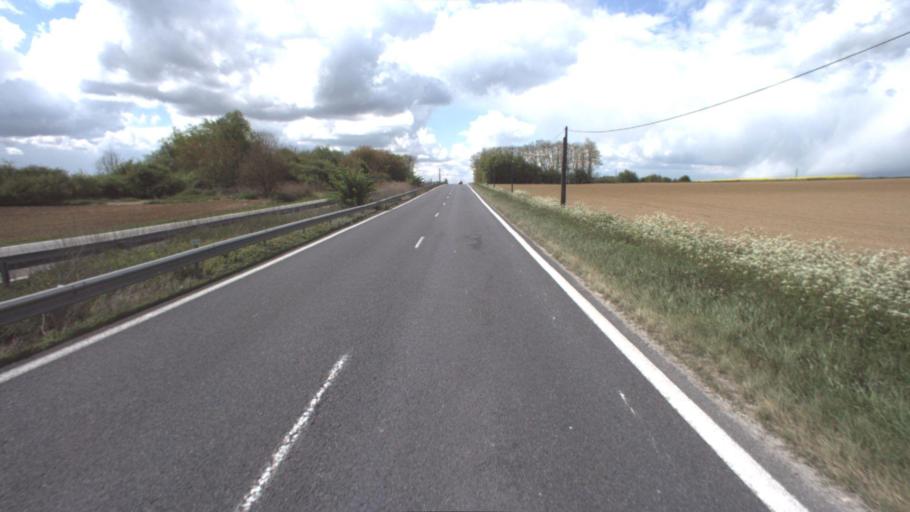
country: FR
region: Ile-de-France
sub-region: Departement de Seine-et-Marne
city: Jouy-le-Chatel
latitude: 48.6846
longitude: 3.0775
